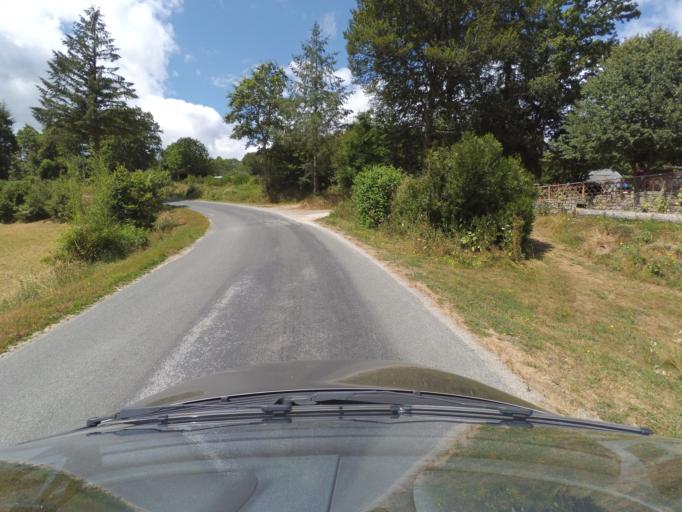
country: FR
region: Limousin
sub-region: Departement de la Creuse
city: Banize
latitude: 45.7965
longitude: 1.9351
